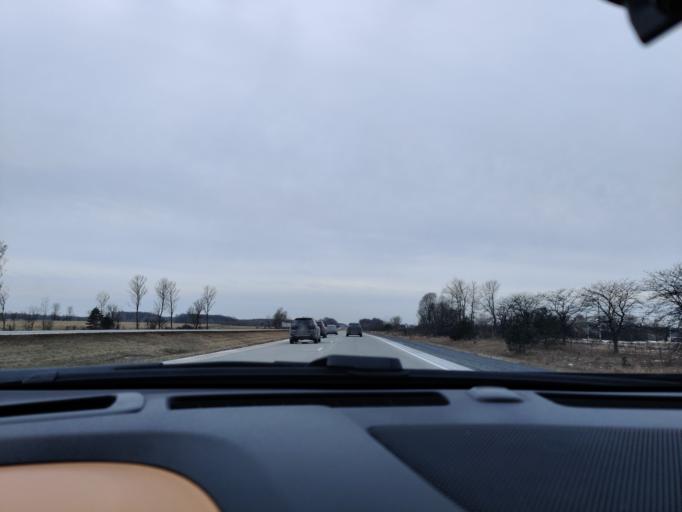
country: US
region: New York
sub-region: St. Lawrence County
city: Massena
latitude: 45.0429
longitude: -74.9184
